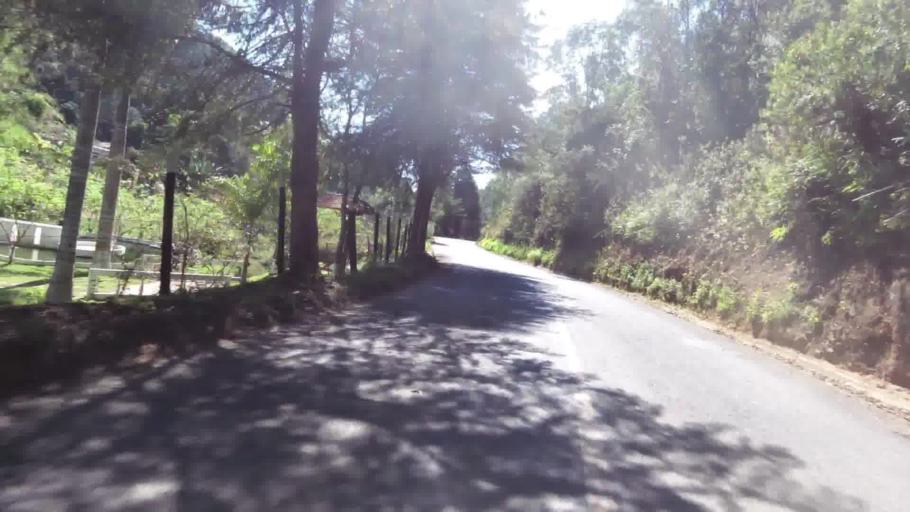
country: BR
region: Espirito Santo
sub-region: Marechal Floriano
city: Marechal Floriano
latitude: -20.4449
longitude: -40.8855
